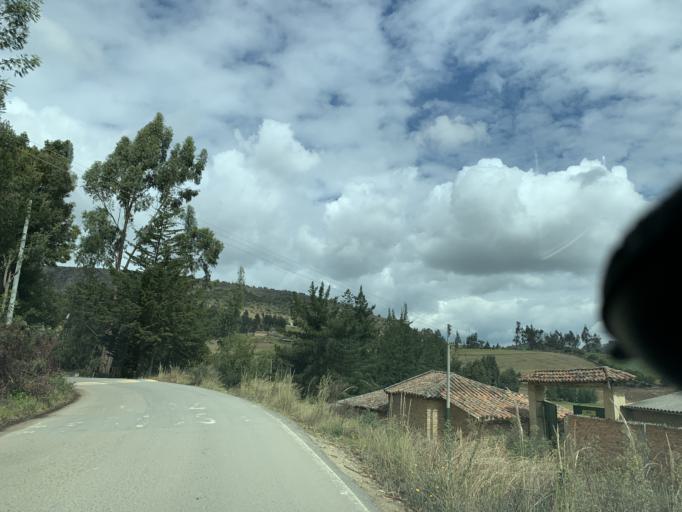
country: CO
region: Boyaca
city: Siachoque
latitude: 5.5692
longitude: -73.2616
